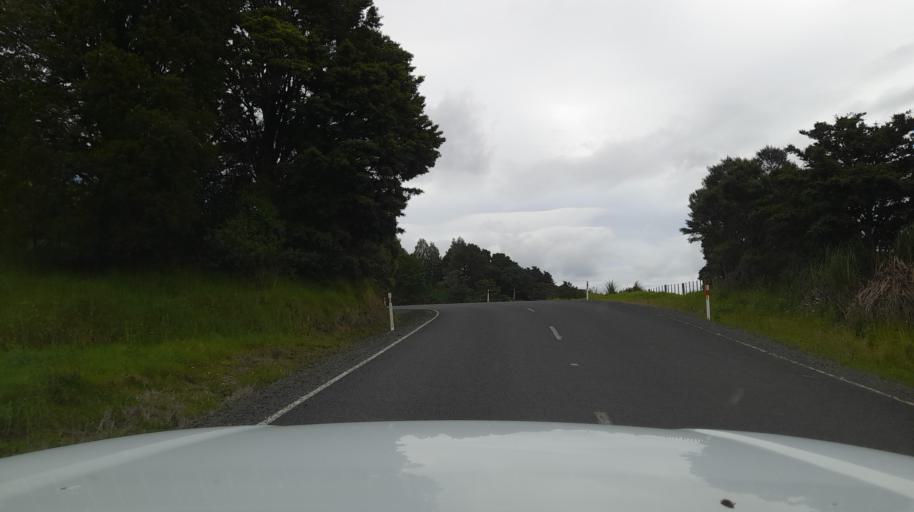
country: NZ
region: Northland
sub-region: Far North District
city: Kaitaia
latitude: -35.3046
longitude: 173.3464
